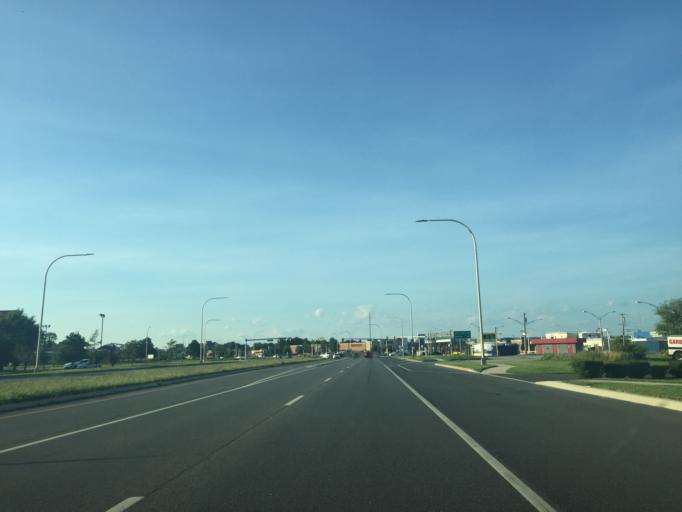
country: US
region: Delaware
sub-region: Kent County
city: Dover
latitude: 39.1556
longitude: -75.5126
